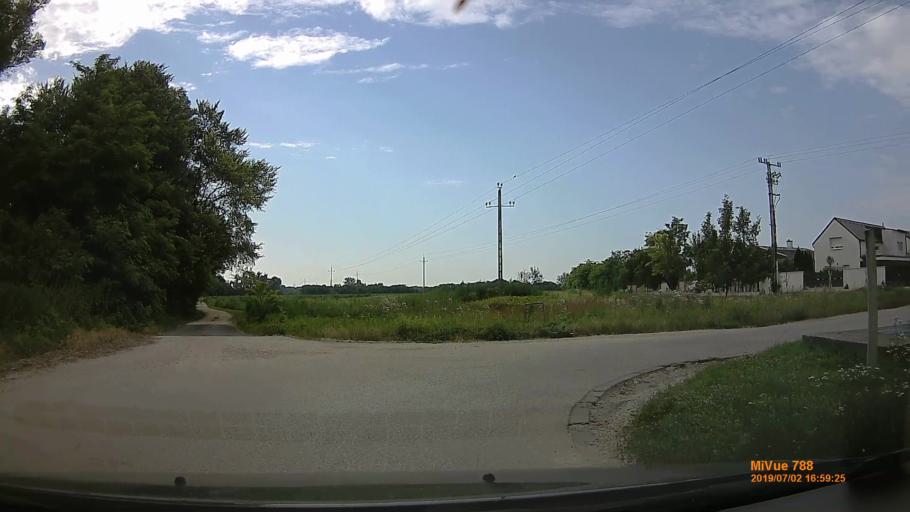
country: HU
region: Gyor-Moson-Sopron
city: Mosonmagyarovar
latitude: 47.8866
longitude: 17.2853
